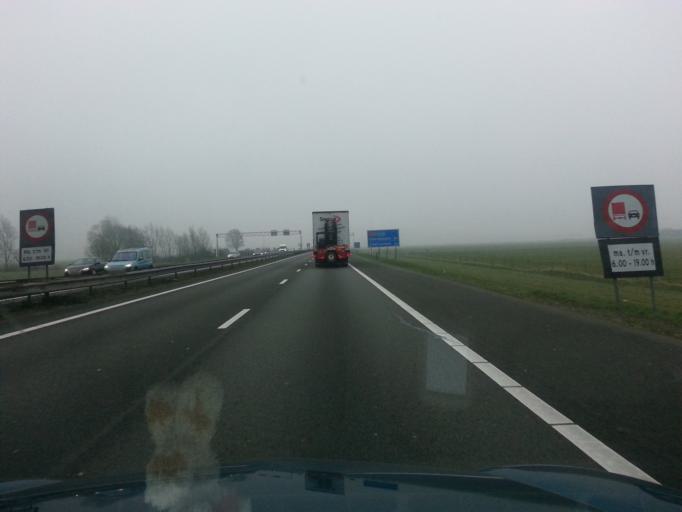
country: NL
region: Gelderland
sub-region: Gemeente Duiven
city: Duiven
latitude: 51.9577
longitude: 6.0345
